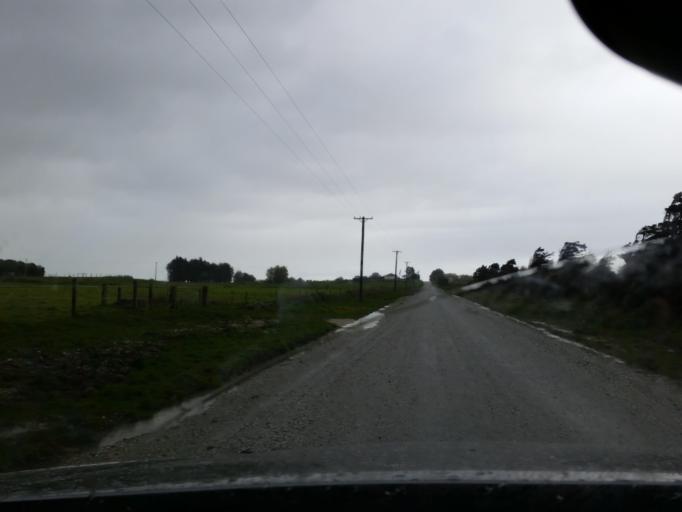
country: NZ
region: Southland
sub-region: Invercargill City
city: Invercargill
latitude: -46.4277
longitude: 168.5061
